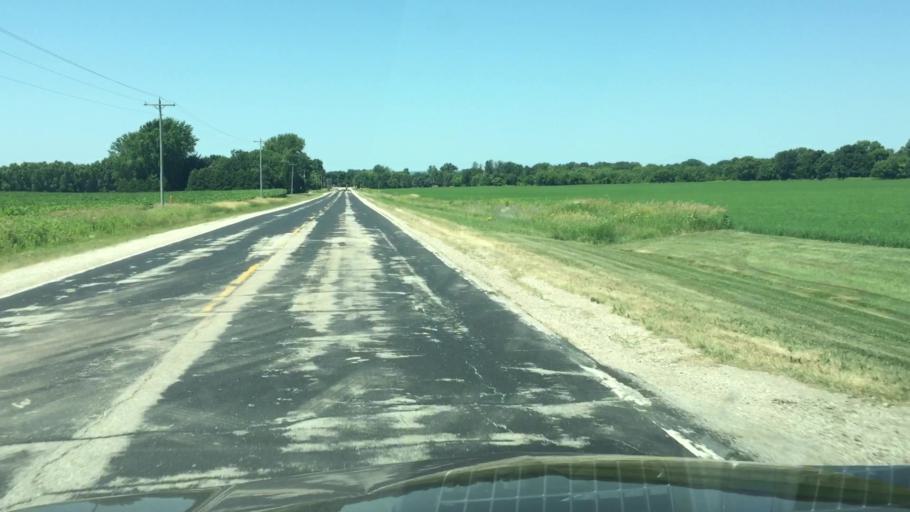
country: US
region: Wisconsin
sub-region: Fond du Lac County
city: Saint Peter
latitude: 43.9696
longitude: -88.2963
